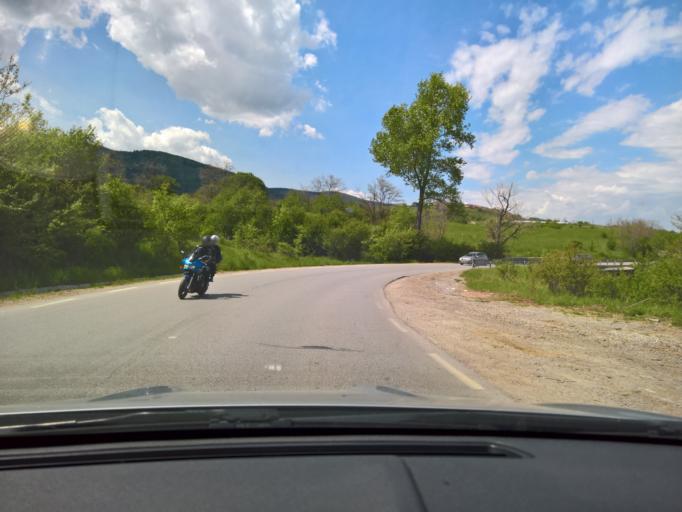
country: BG
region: Sofia-Capital
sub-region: Stolichna Obshtina
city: Sofia
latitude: 42.5718
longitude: 23.3594
